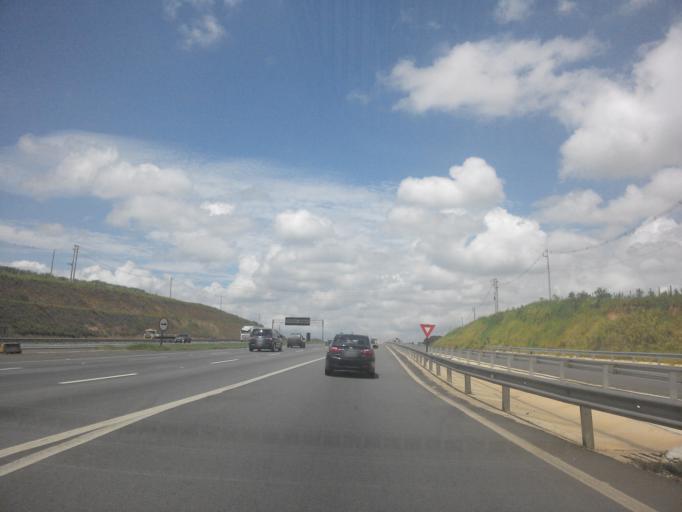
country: BR
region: Sao Paulo
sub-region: Campinas
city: Campinas
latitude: -22.8554
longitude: -47.0249
